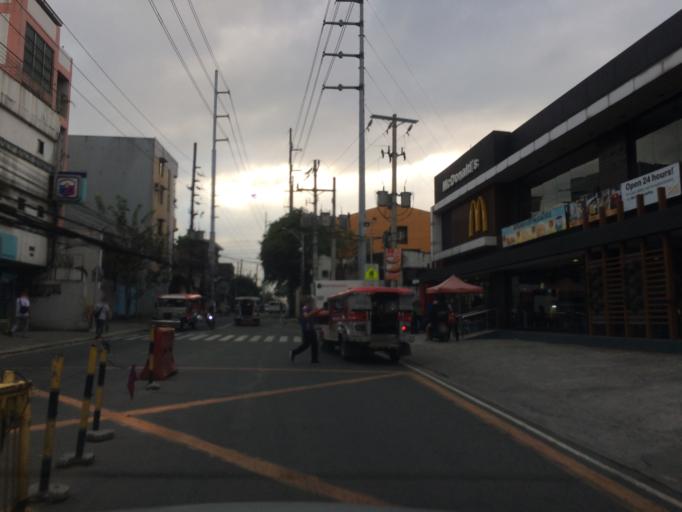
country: PH
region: Calabarzon
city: Bagong Pagasa
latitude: 14.6755
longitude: 121.0453
